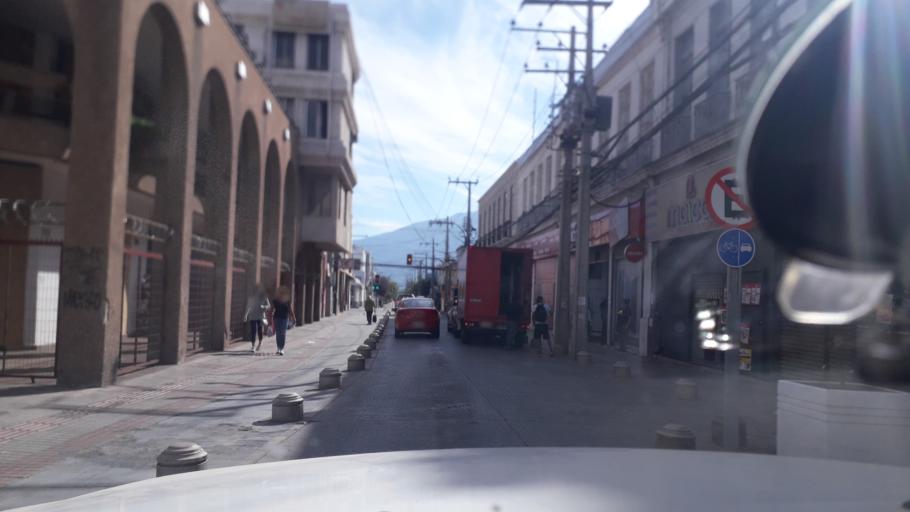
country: CL
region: Valparaiso
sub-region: Provincia de San Felipe
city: San Felipe
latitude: -32.7500
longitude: -70.7260
